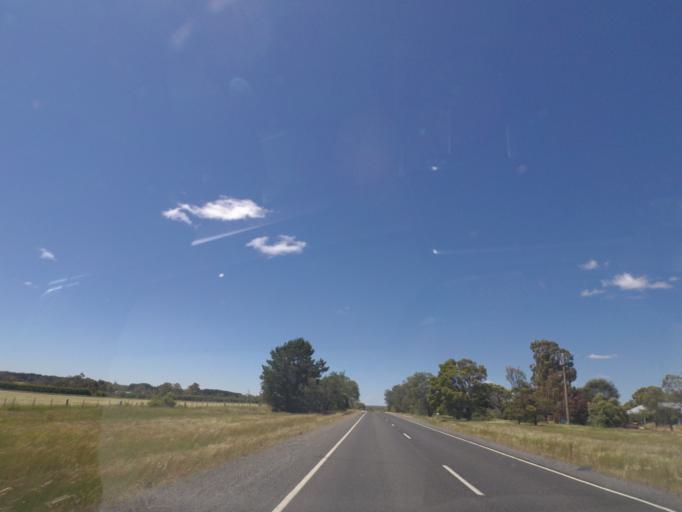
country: AU
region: Victoria
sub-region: Mount Alexander
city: Castlemaine
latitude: -37.2174
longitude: 144.3465
